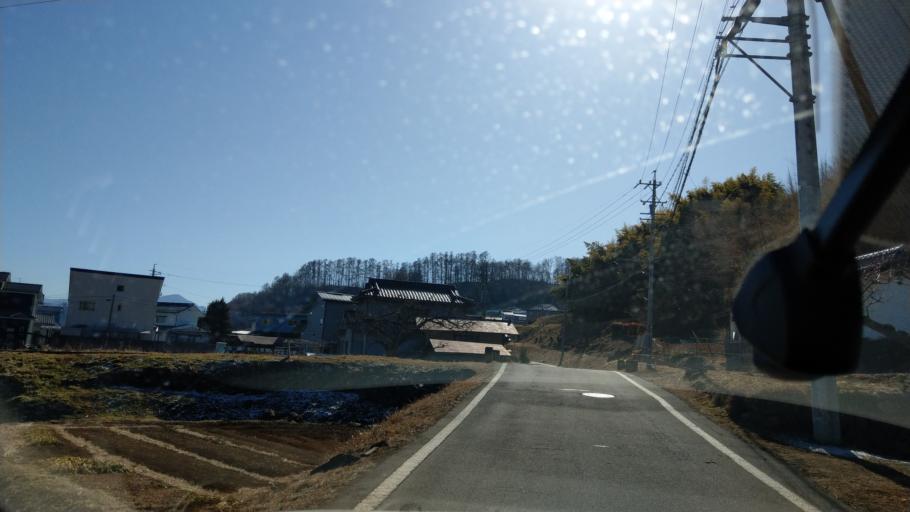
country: JP
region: Nagano
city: Saku
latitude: 36.2227
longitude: 138.4458
